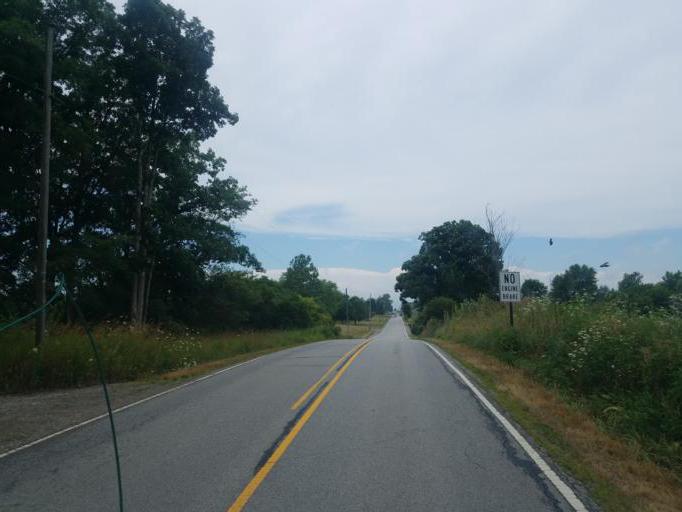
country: US
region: Indiana
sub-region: DeKalb County
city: Butler
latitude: 41.3860
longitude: -84.8651
